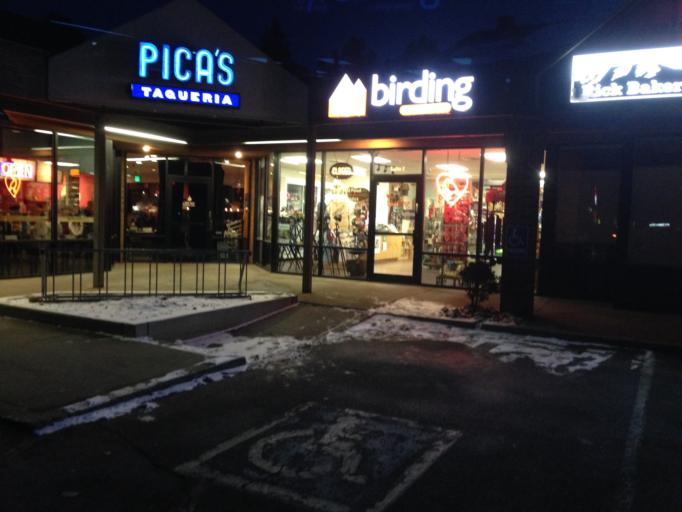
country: US
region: Colorado
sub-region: Boulder County
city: Boulder
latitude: 40.0140
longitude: -105.2277
